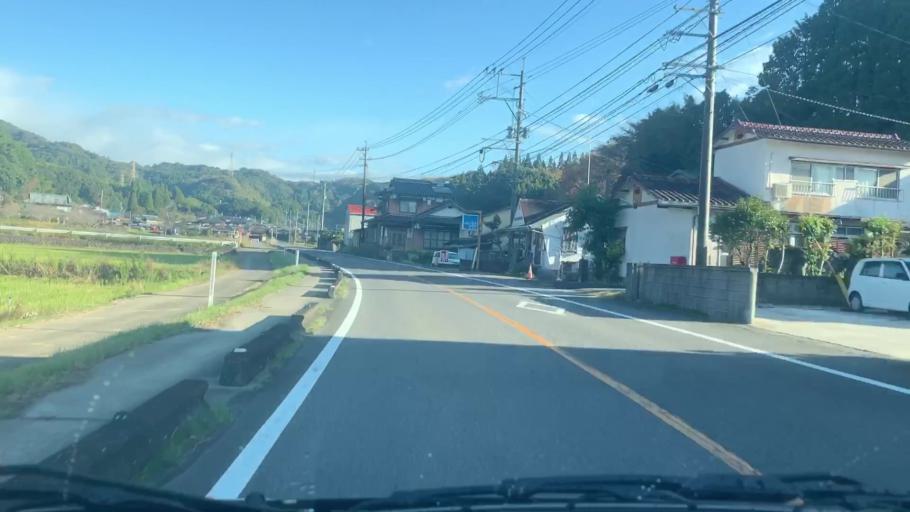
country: JP
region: Saga Prefecture
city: Takeocho-takeo
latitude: 33.2288
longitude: 130.0594
